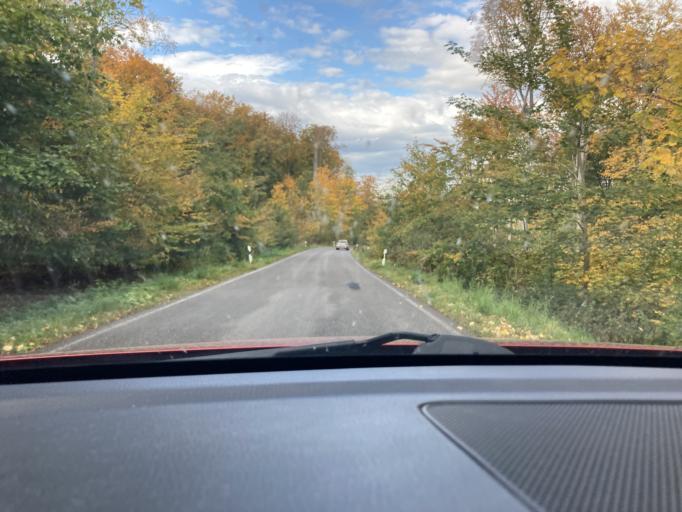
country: DE
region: Thuringia
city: Kleinbodungen
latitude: 51.4951
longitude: 10.5508
